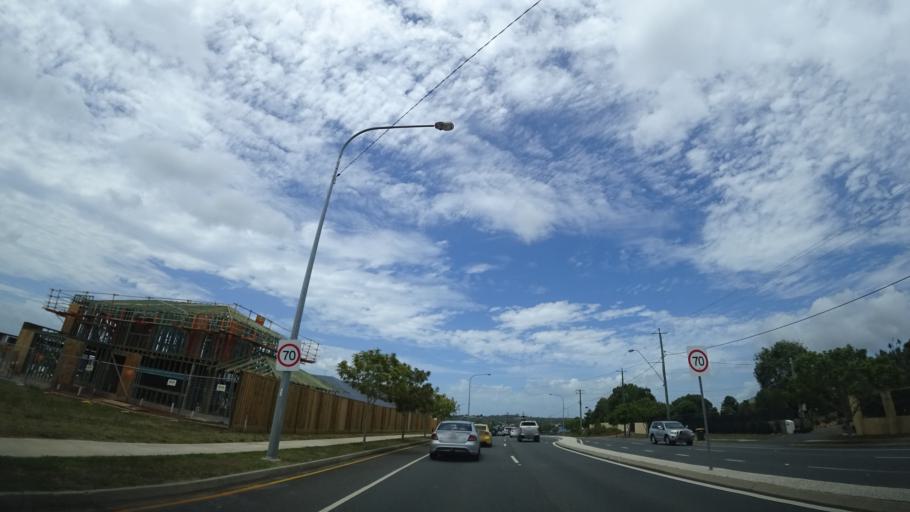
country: AU
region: Queensland
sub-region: Brisbane
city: Bald Hills
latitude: -27.3354
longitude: 152.9997
